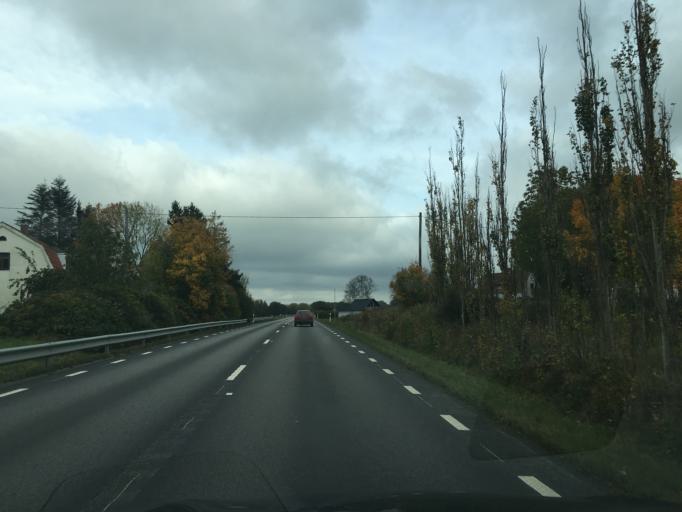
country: SE
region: Skane
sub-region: Tomelilla Kommun
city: Tomelilla
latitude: 55.6453
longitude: 14.0102
